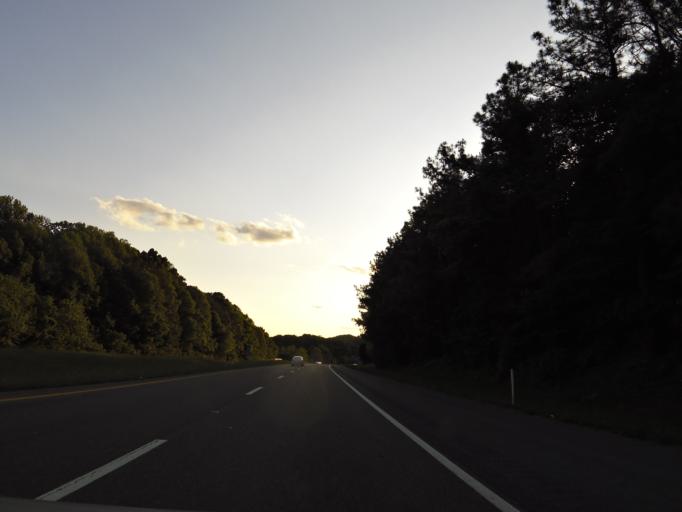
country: US
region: Tennessee
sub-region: Sullivan County
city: Blountville
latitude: 36.5391
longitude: -82.3496
